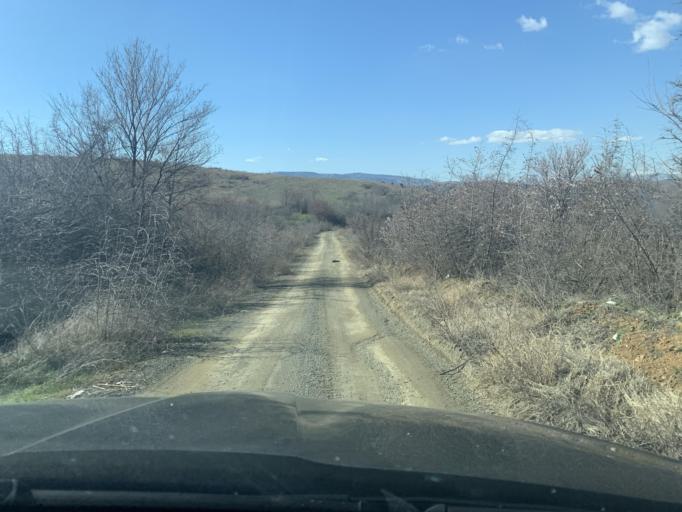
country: MK
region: Demir Kapija
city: Demir Kapija
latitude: 41.4139
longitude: 22.2159
